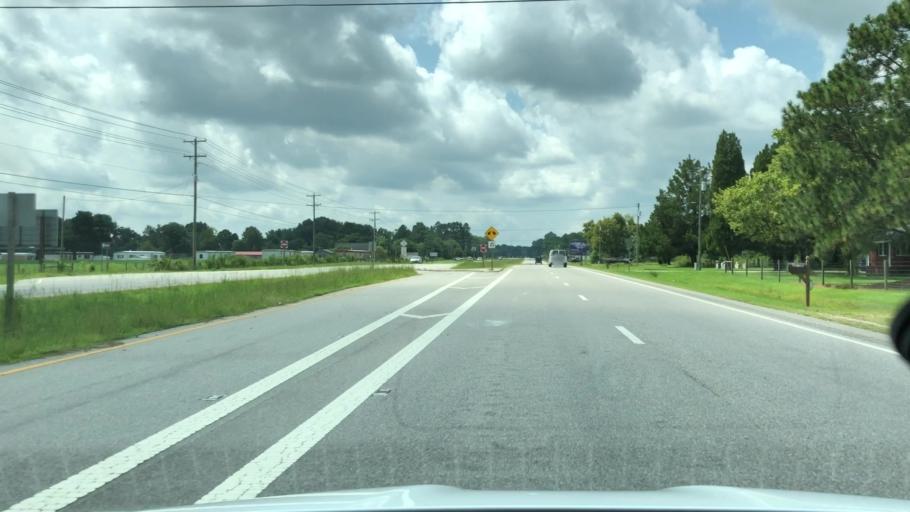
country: US
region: North Carolina
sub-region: Beaufort County
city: Washington
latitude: 35.4845
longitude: -77.1113
